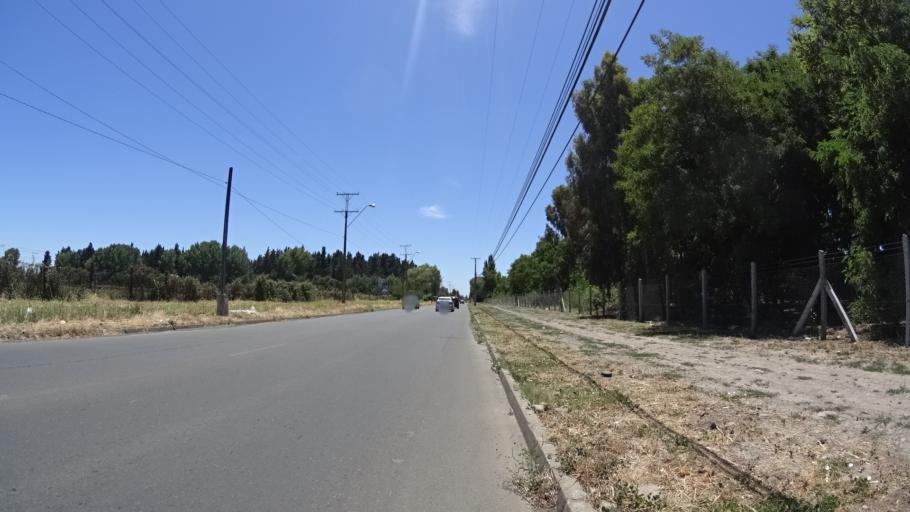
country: CL
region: Biobio
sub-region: Provincia de Nuble
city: Chillan
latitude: -36.5976
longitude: -72.0747
